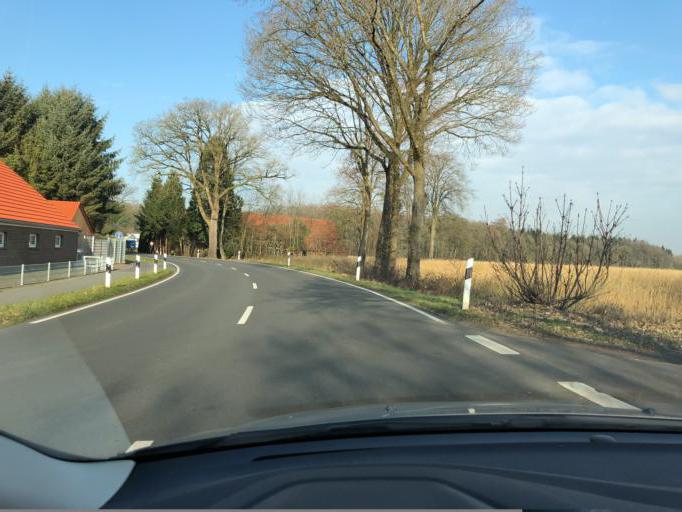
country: DE
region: Lower Saxony
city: Westerstede
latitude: 53.2641
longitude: 7.9140
